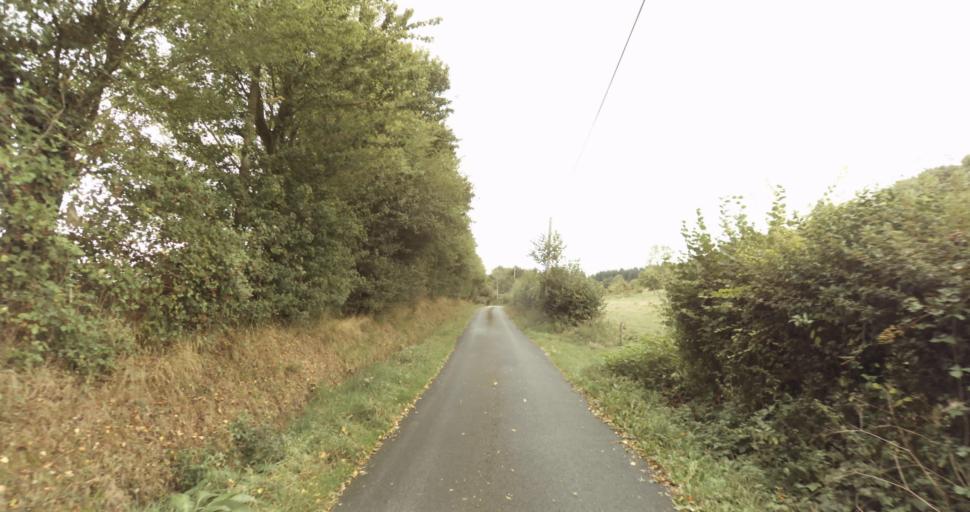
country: FR
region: Lower Normandy
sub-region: Departement de l'Orne
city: Vimoutiers
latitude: 48.8890
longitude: 0.1696
